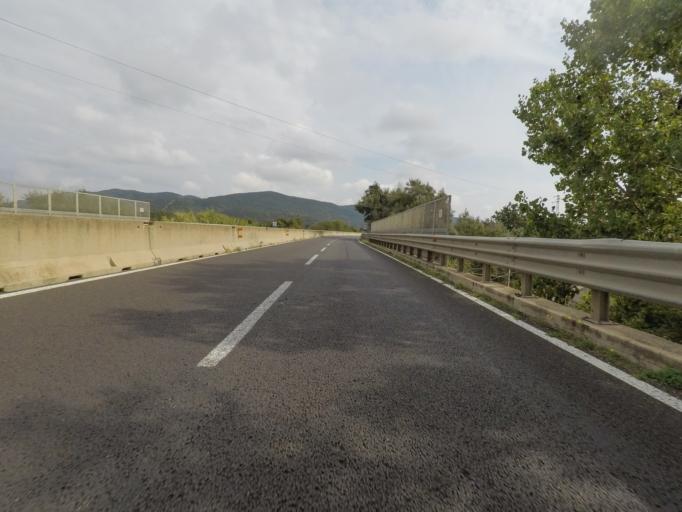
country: IT
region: Tuscany
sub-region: Provincia di Grosseto
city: Albinia
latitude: 42.4784
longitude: 11.2283
